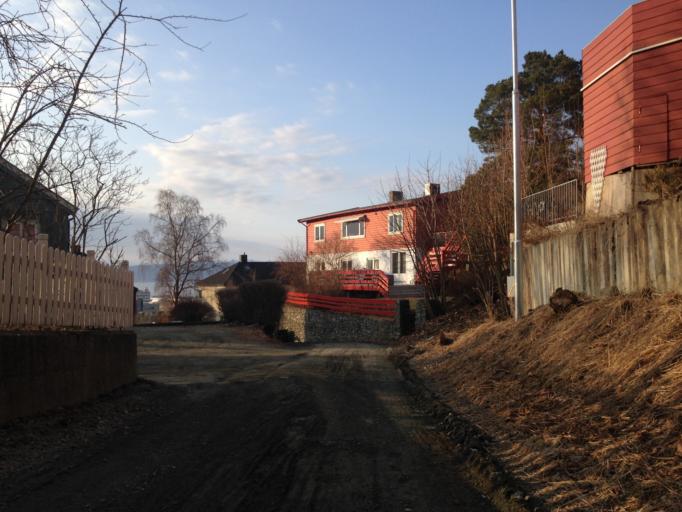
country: NO
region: Sor-Trondelag
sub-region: Trondheim
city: Trondheim
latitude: 63.4331
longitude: 10.4210
